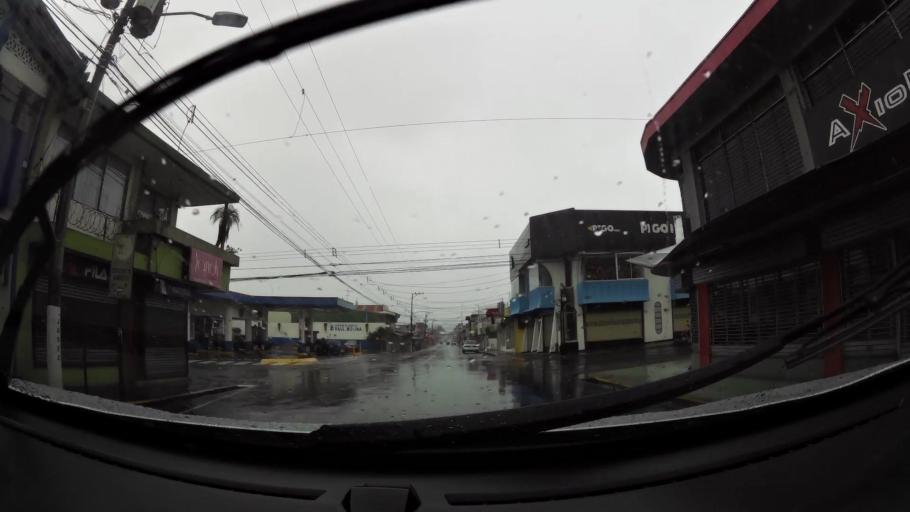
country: CR
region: Cartago
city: Cartago
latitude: 9.8660
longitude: -83.9235
